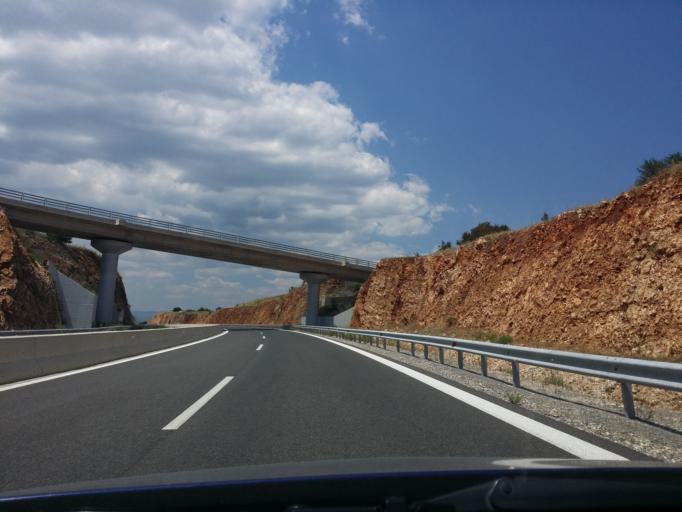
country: GR
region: Peloponnese
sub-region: Nomos Arkadias
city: Megalopoli
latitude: 37.2871
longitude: 22.2144
